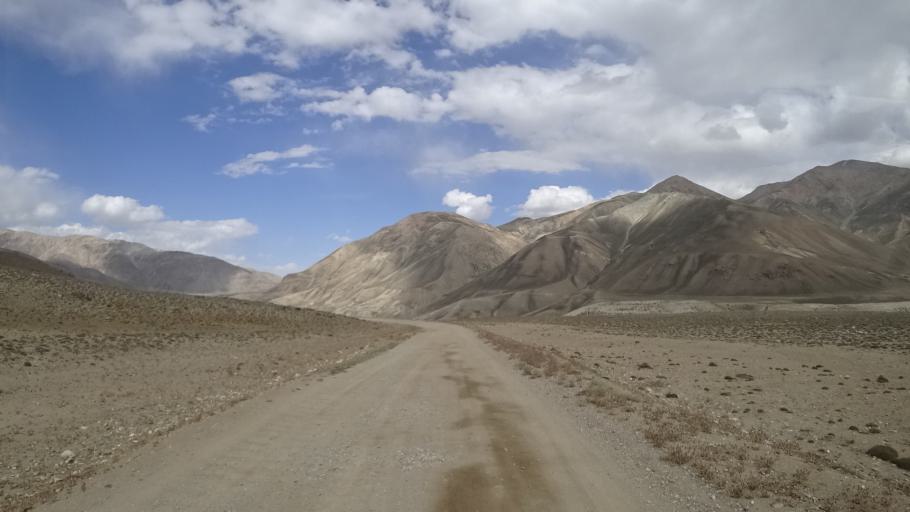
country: AF
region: Badakhshan
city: Khandud
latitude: 37.1938
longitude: 72.7675
